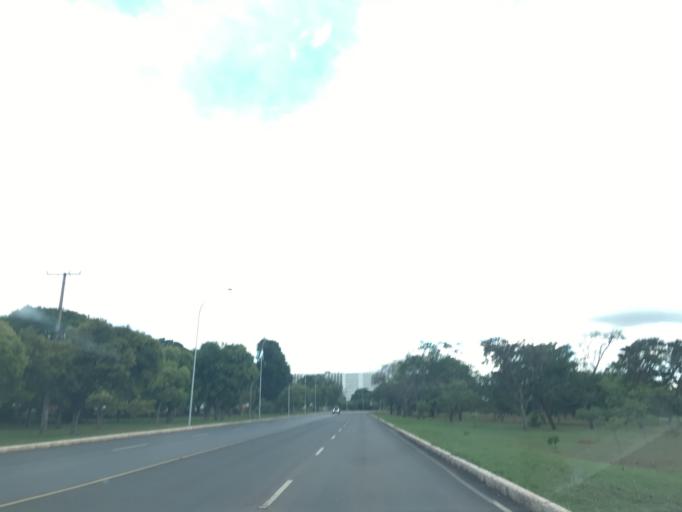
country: BR
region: Federal District
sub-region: Brasilia
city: Brasilia
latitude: -15.7938
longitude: -47.9095
